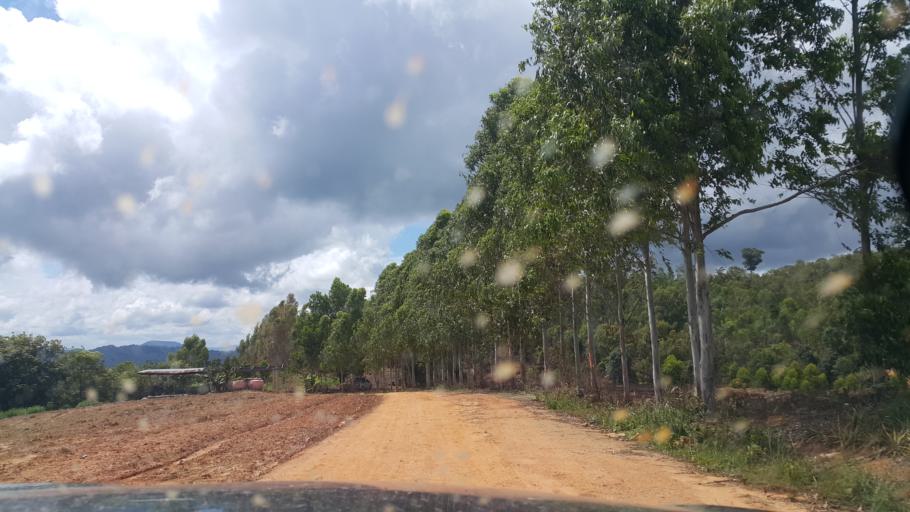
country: TH
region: Loei
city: Na Haeo
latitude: 17.5981
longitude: 100.9004
